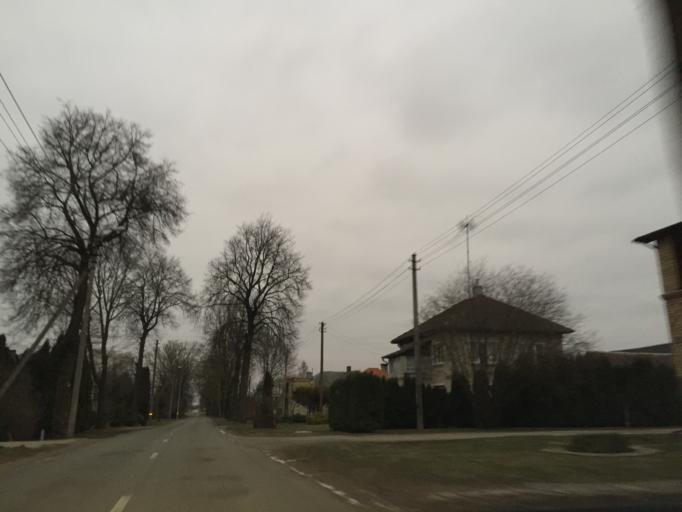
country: LT
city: Zagare
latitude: 56.3449
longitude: 23.3086
